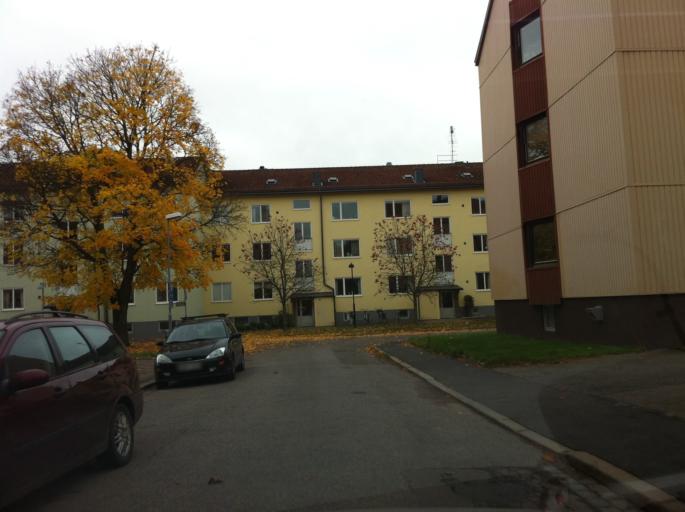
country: SE
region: OEstergoetland
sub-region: Linkopings Kommun
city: Linkoping
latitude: 58.4060
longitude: 15.6015
